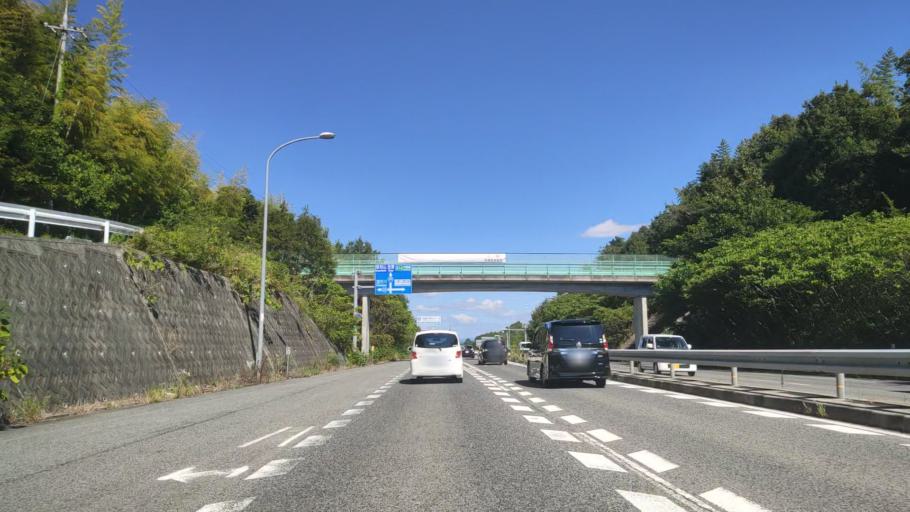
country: JP
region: Hyogo
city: Ono
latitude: 34.8282
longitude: 134.9495
